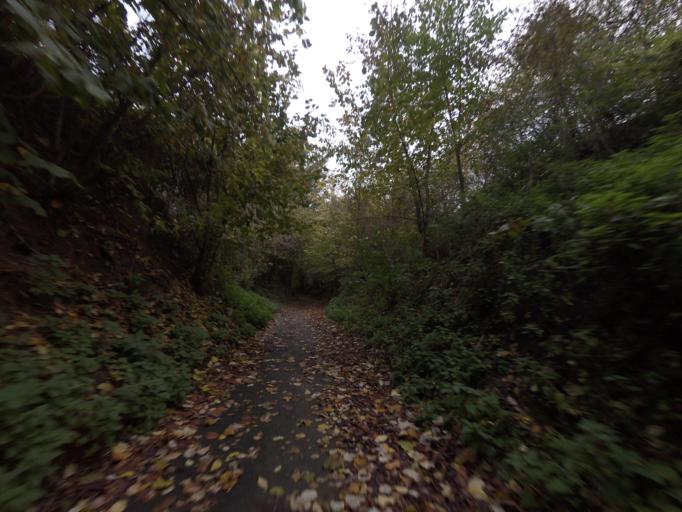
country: BE
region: Flanders
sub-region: Provincie Vlaams-Brabant
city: Kraainem
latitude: 50.8735
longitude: 4.4608
